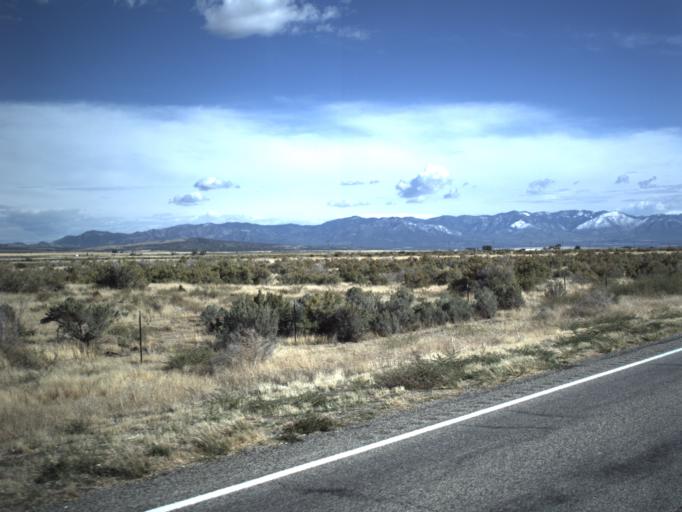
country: US
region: Utah
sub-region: Millard County
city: Delta
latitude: 39.2343
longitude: -112.4293
